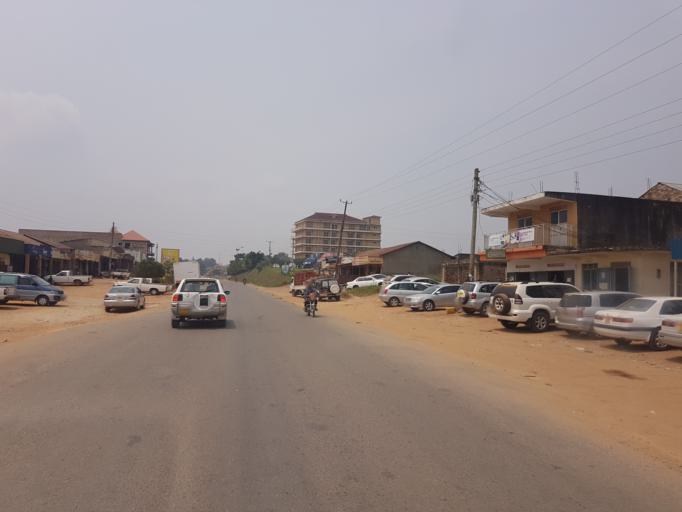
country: UG
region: Western Region
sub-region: Bushenyi District
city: Bushenyi
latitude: -0.5407
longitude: 30.1889
